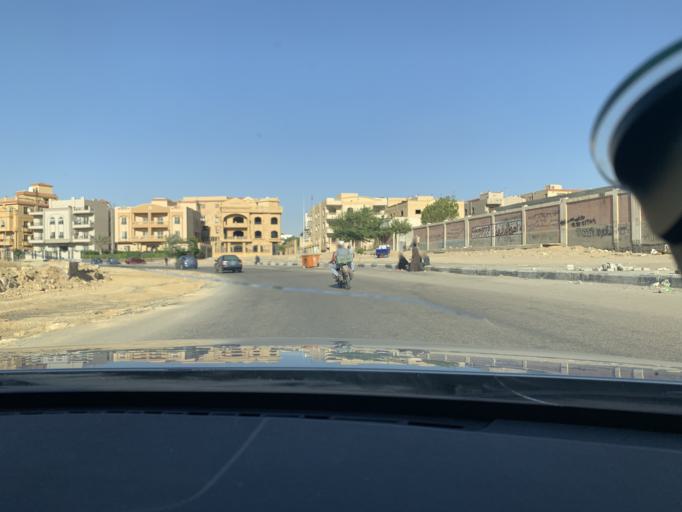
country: EG
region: Muhafazat al Qalyubiyah
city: Al Khankah
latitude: 30.0528
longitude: 31.4678
